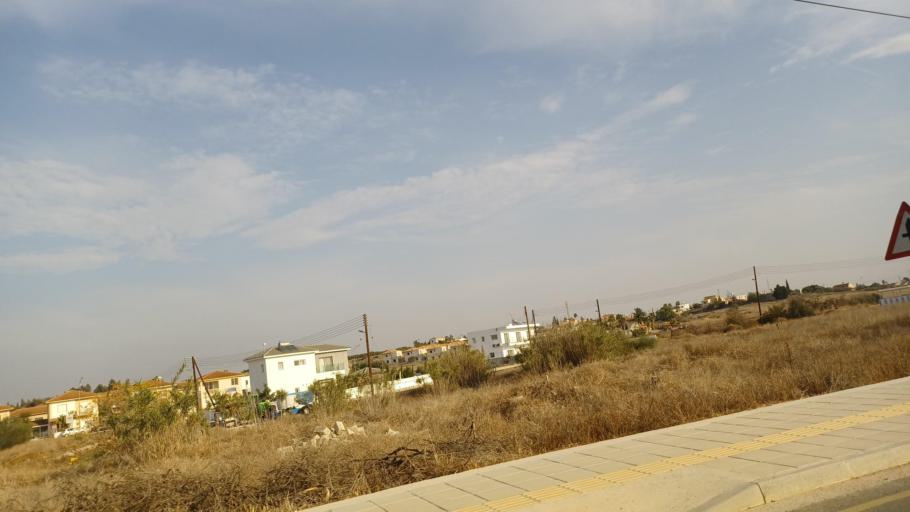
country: CY
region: Ammochostos
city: Acheritou
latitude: 35.0788
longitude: 33.8734
